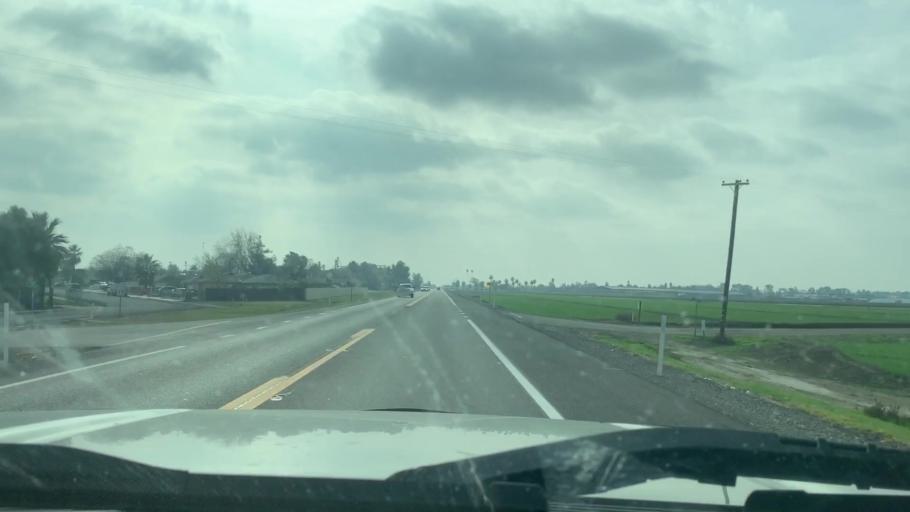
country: US
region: California
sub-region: Kings County
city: Stratford
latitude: 36.1970
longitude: -119.8224
